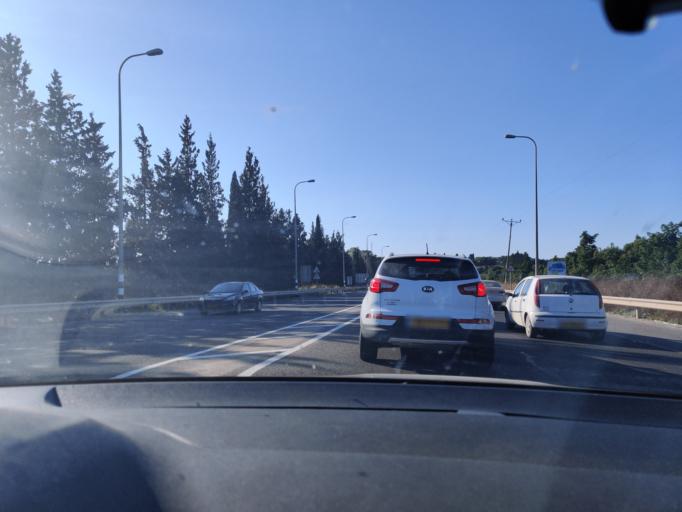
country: PS
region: West Bank
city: Nazlat `Isa
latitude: 32.4449
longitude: 35.0216
